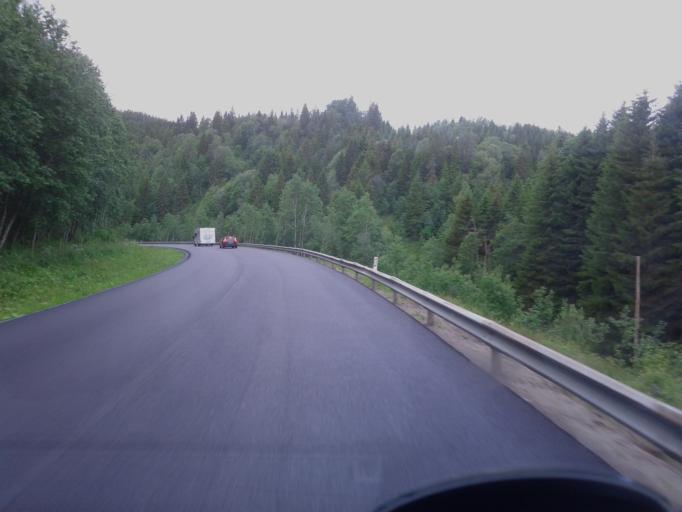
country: NO
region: Nord-Trondelag
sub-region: Grong
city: Grong
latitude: 64.5287
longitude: 12.3916
